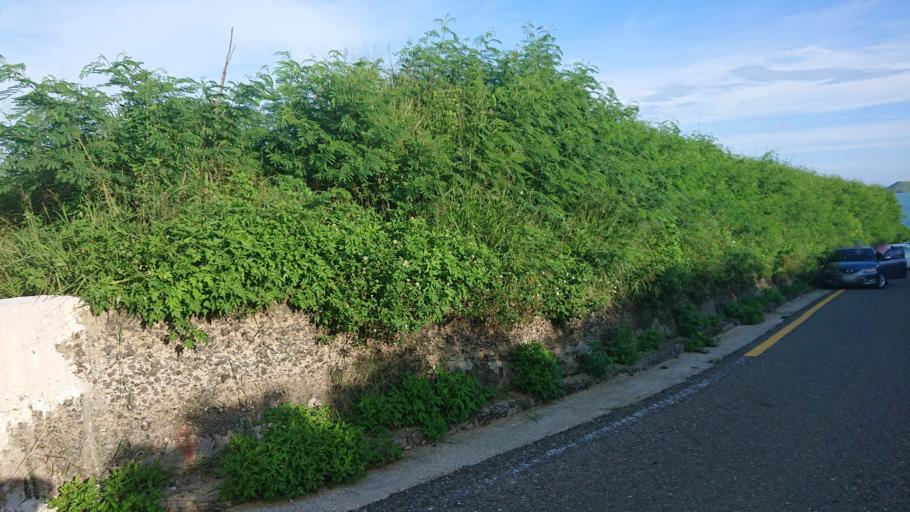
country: TW
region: Taiwan
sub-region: Penghu
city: Ma-kung
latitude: 23.5964
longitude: 119.5165
